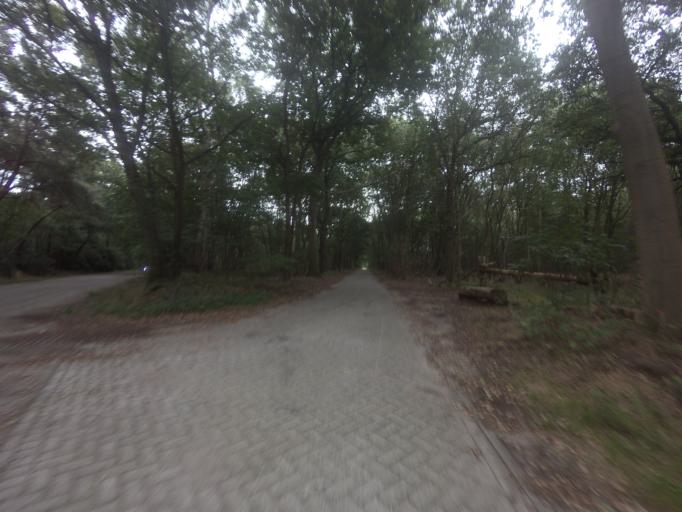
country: NL
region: Overijssel
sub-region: Gemeente Raalte
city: Raalte
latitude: 52.3159
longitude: 6.2935
